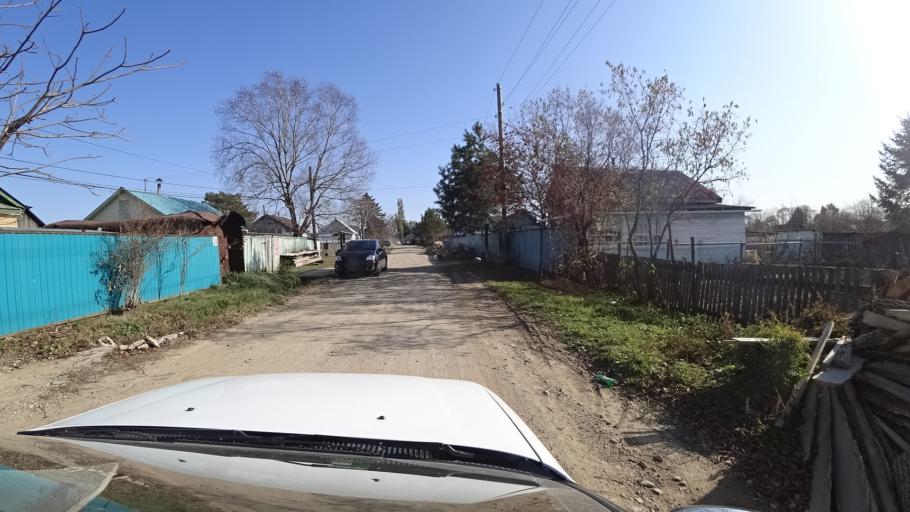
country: RU
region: Primorskiy
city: Dal'nerechensk
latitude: 45.9270
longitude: 133.7176
